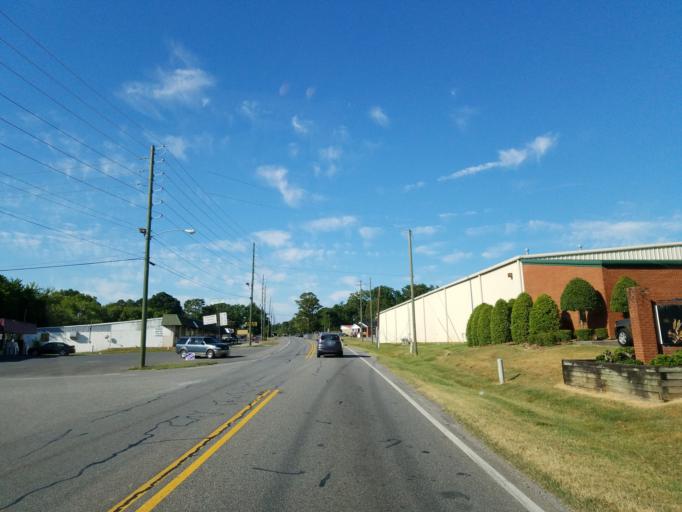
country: US
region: Georgia
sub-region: Gordon County
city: Calhoun
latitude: 34.5170
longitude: -84.9448
